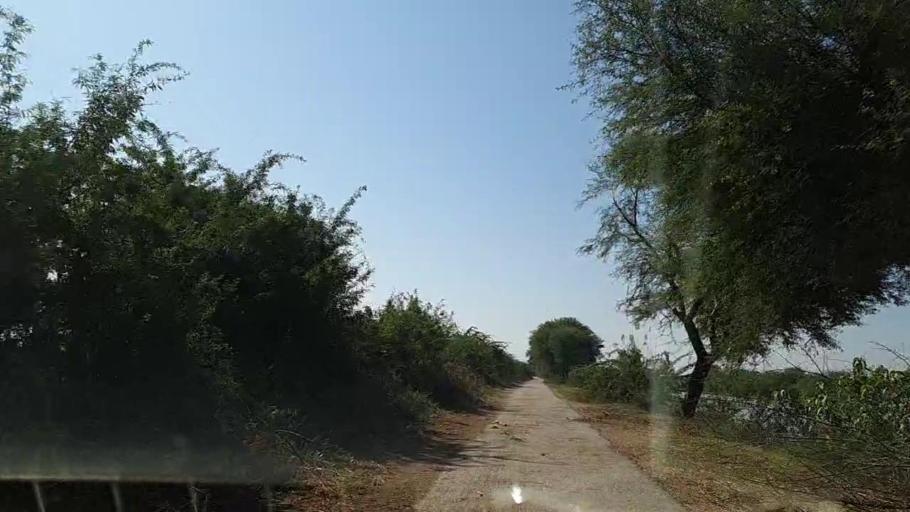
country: PK
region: Sindh
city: Chuhar Jamali
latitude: 24.5790
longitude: 68.0466
